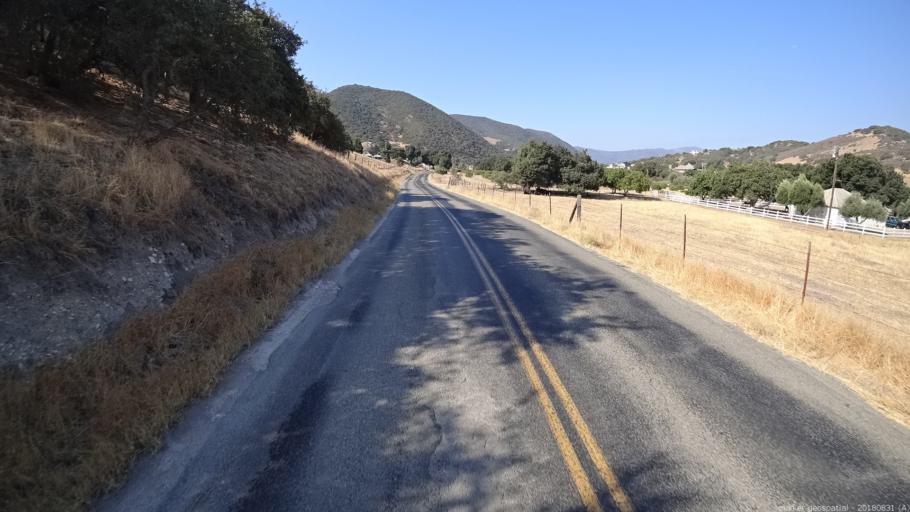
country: US
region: California
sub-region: Monterey County
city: King City
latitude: 36.1602
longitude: -121.1647
